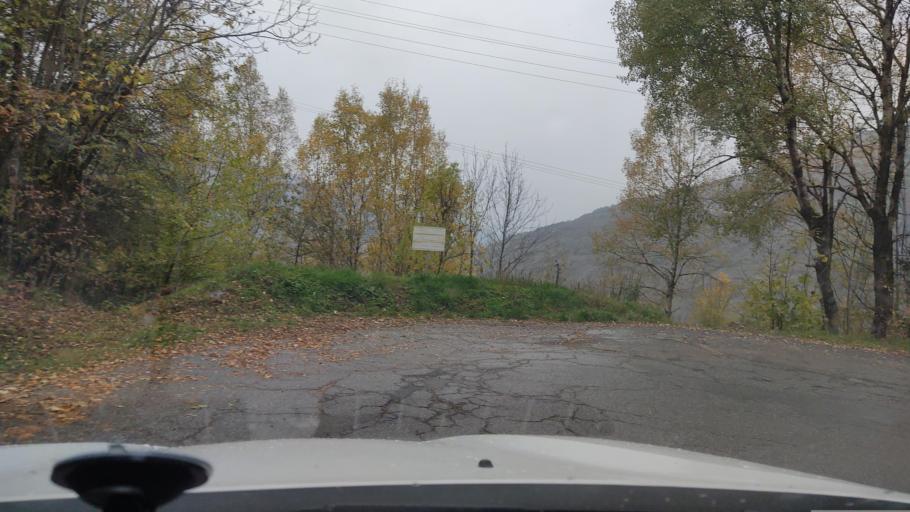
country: FR
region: Rhone-Alpes
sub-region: Departement de la Savoie
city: Bourg-Saint-Maurice
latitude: 45.5975
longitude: 6.7695
